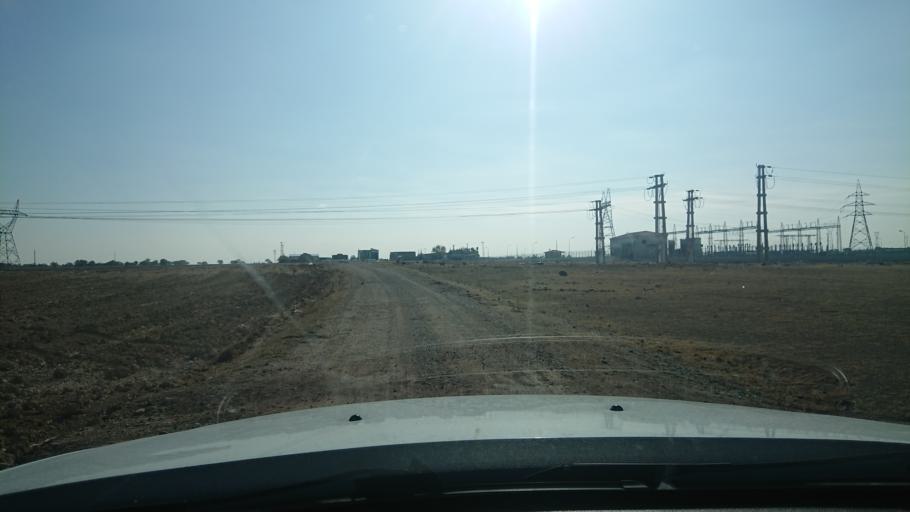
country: TR
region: Aksaray
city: Sultanhani
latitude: 38.2550
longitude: 33.4716
